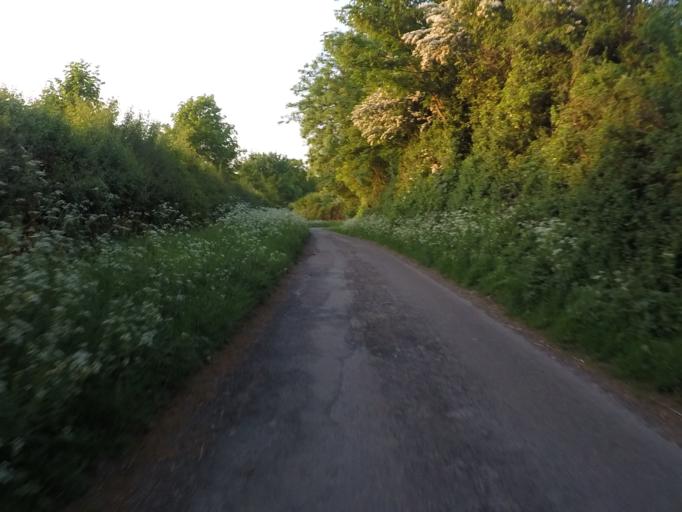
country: GB
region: England
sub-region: Oxfordshire
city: North Leigh
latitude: 51.8281
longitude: -1.4774
